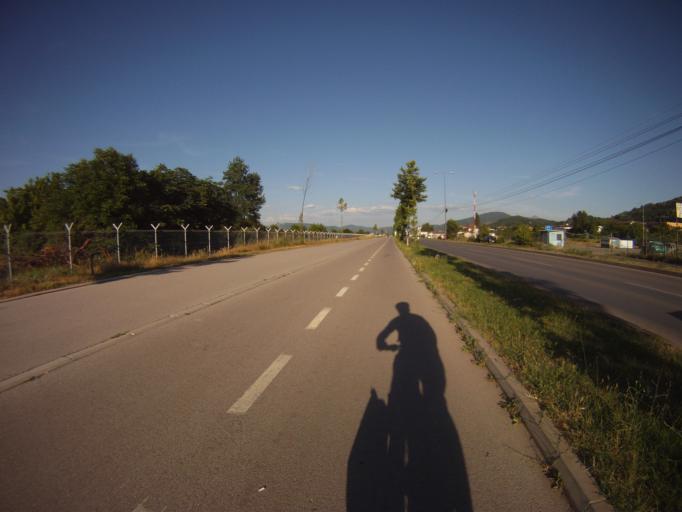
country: RS
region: Central Serbia
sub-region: Nisavski Okrug
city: Nis
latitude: 43.3097
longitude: 21.9398
